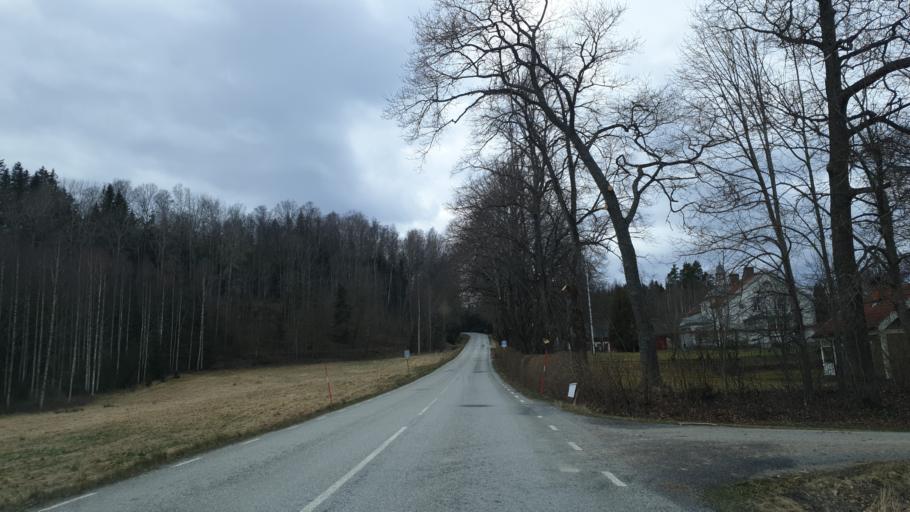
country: SE
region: OErebro
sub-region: Nora Kommun
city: As
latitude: 59.5603
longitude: 15.0192
